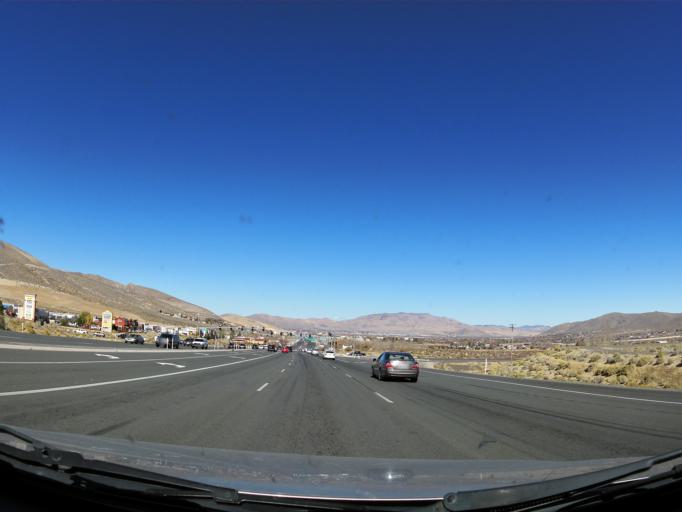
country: US
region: Nevada
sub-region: Douglas County
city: Indian Hills
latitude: 39.1088
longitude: -119.7738
